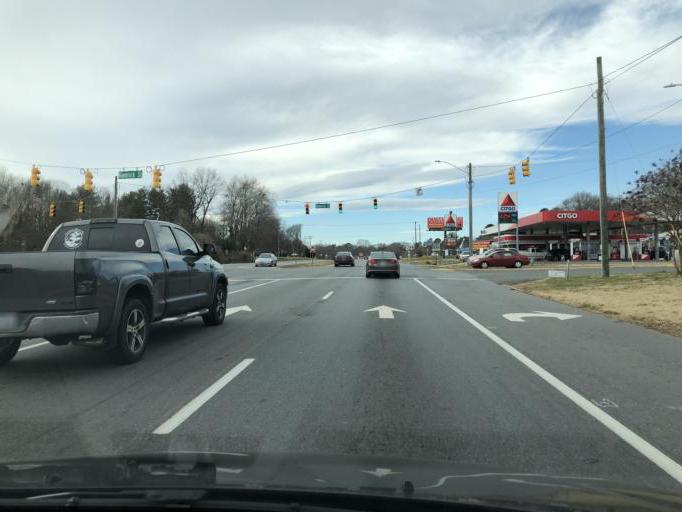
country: US
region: North Carolina
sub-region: Cleveland County
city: Shelby
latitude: 35.2809
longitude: -81.5492
